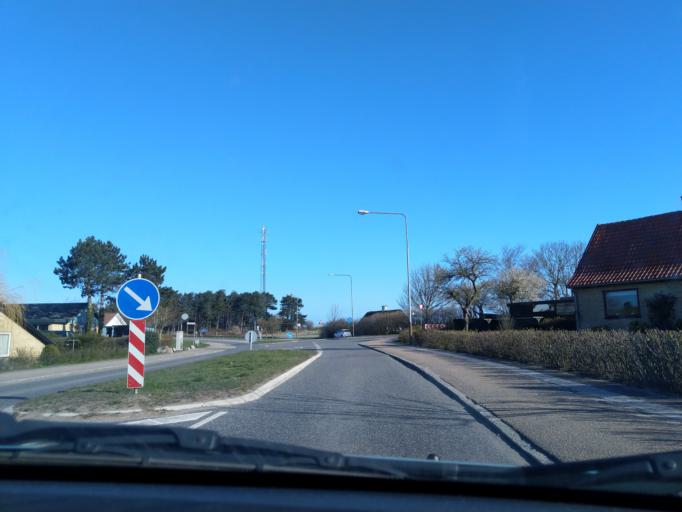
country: DK
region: Zealand
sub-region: Kalundborg Kommune
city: Kalundborg
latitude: 55.7103
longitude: 11.0209
